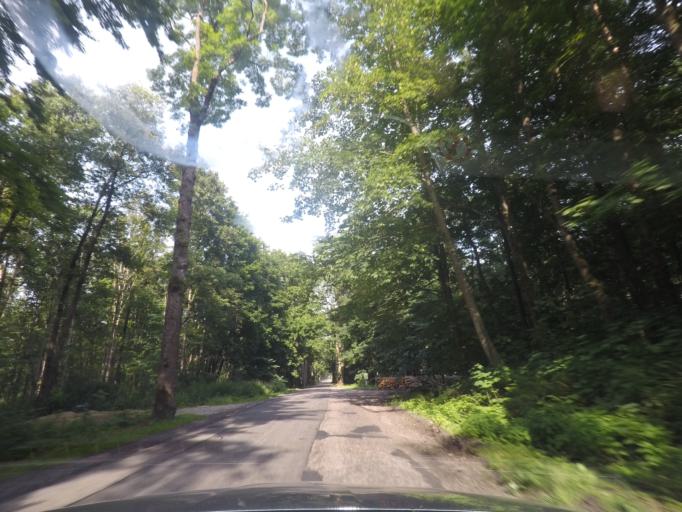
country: PL
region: Pomeranian Voivodeship
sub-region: Powiat slupski
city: Glowczyce
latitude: 54.6068
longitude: 17.3264
